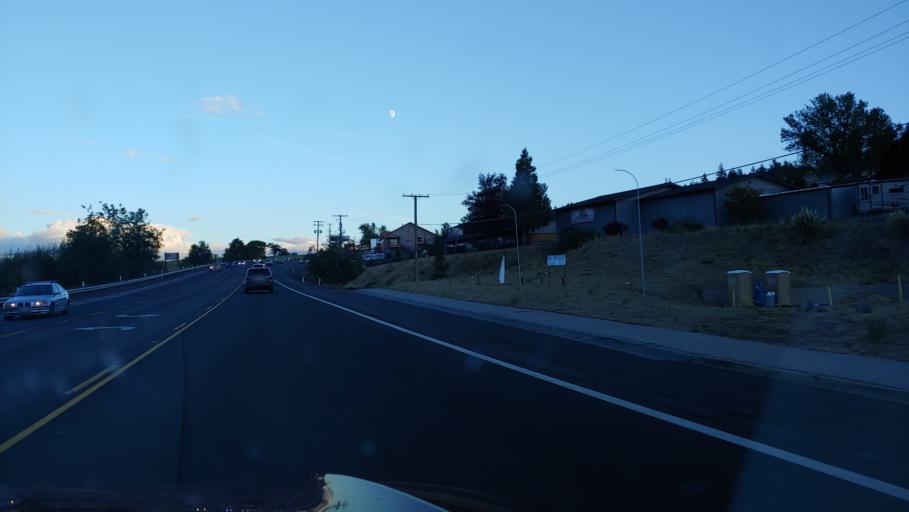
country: US
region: Oregon
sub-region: Jackson County
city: Ashland
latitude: 42.2182
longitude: -122.7360
